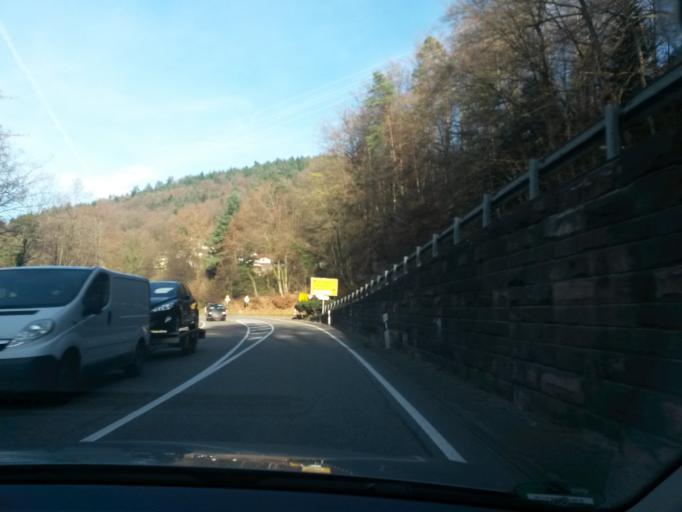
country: DE
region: Baden-Wuerttemberg
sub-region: Karlsruhe Region
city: Neuenburg
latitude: 48.8391
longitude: 8.6003
